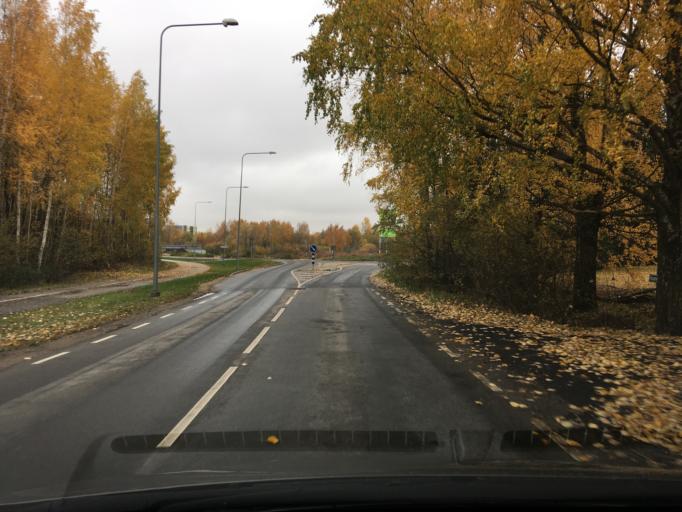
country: EE
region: Tartu
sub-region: Tartu linn
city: Tartu
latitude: 58.3663
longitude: 26.7588
